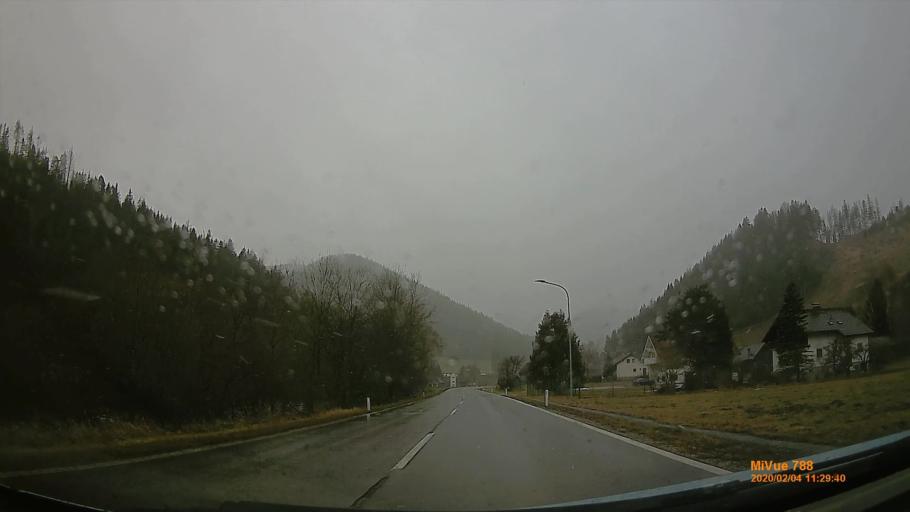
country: AT
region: Styria
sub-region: Politischer Bezirk Bruck-Muerzzuschlag
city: Kapellen
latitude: 47.6543
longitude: 15.6126
